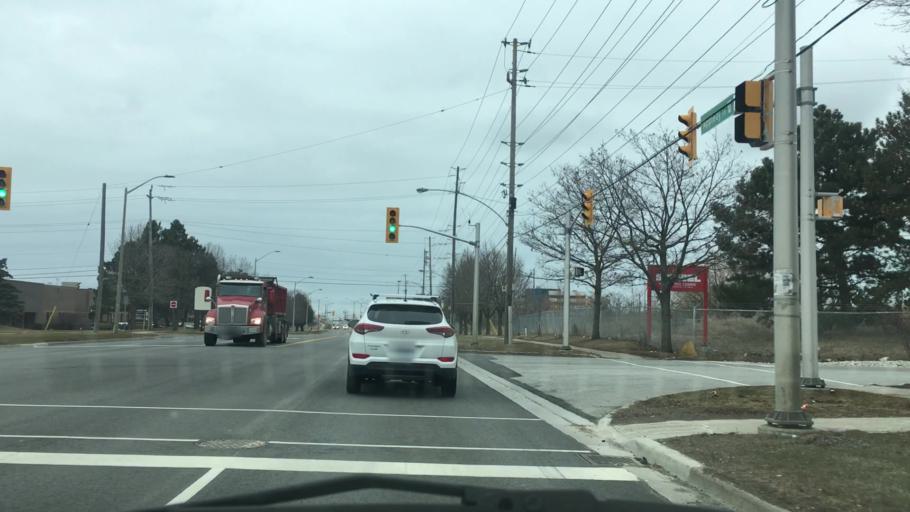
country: CA
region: Ontario
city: Burlington
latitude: 43.3853
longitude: -79.7785
